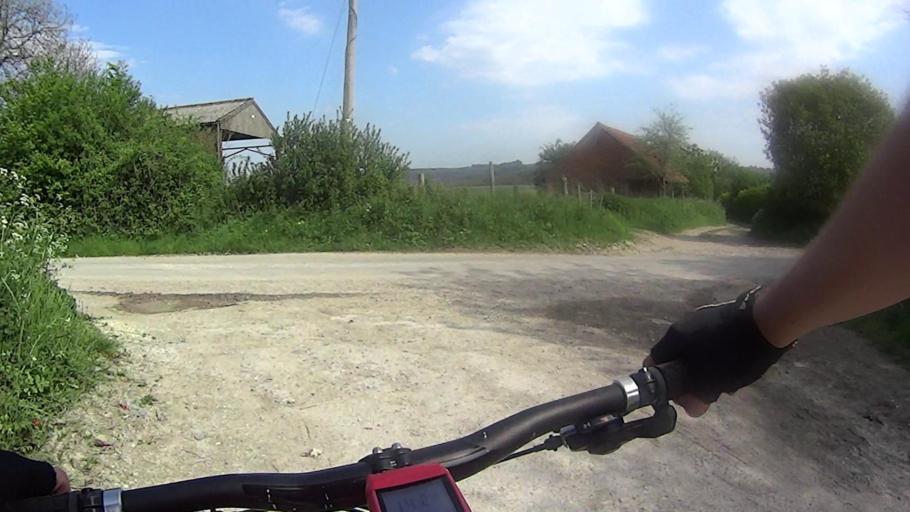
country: GB
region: England
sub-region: Hampshire
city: Petersfield
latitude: 50.9663
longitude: -0.9022
